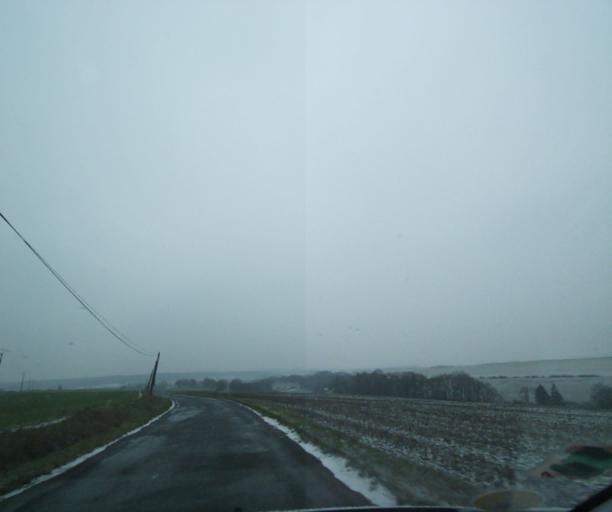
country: FR
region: Champagne-Ardenne
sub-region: Departement de la Haute-Marne
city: Wassy
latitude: 48.4703
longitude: 4.9884
